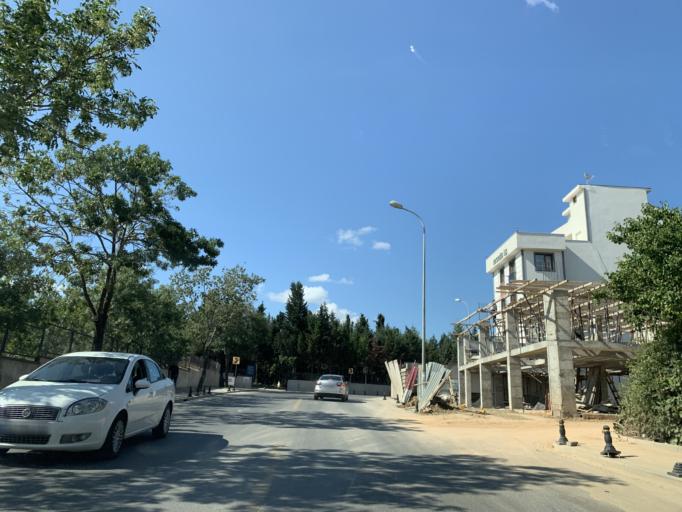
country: TR
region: Istanbul
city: Pendik
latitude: 40.8854
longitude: 29.2833
